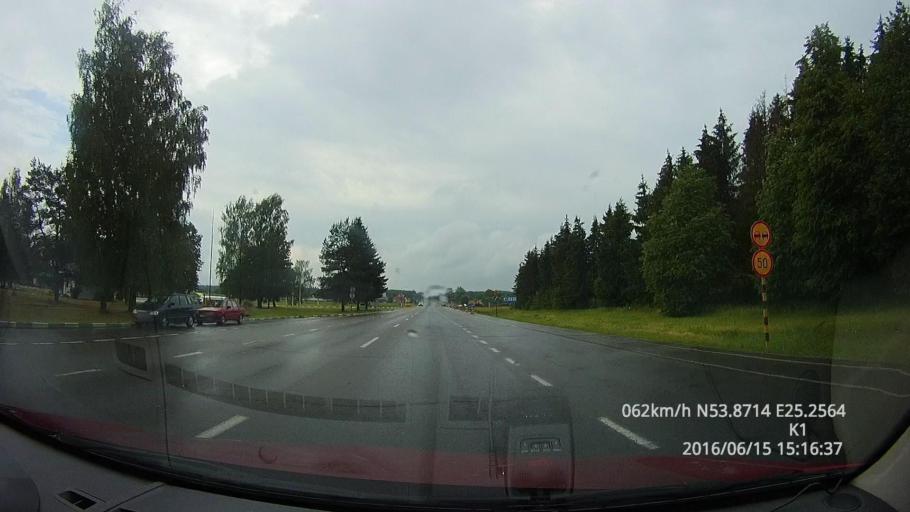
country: BY
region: Grodnenskaya
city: Lida
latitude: 53.8713
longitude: 25.2561
